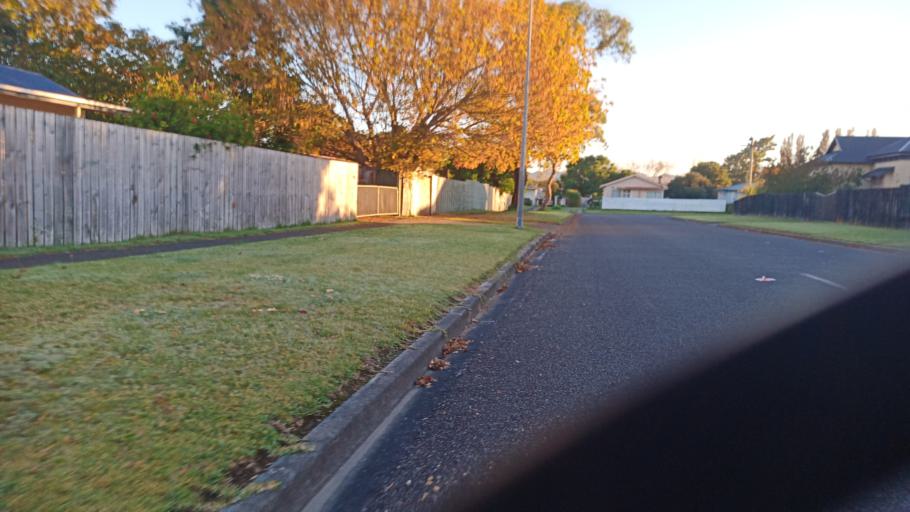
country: NZ
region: Gisborne
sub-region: Gisborne District
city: Gisborne
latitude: -38.6623
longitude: 177.9917
